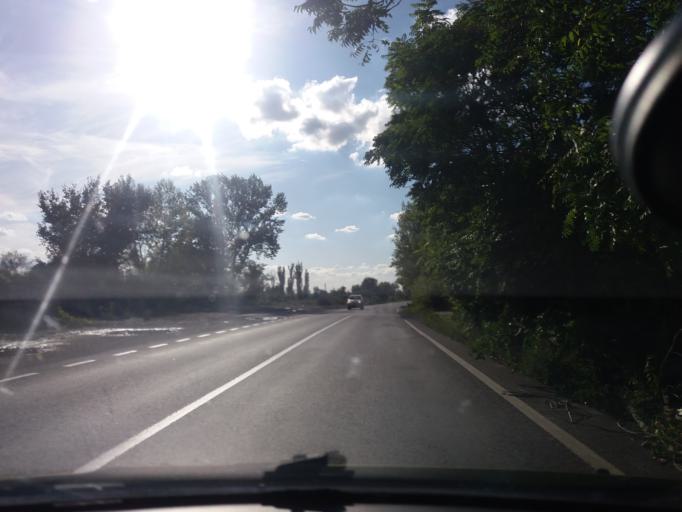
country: RO
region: Arad
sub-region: Comuna Zabrani
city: Neudorf
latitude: 46.1072
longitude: 21.6229
